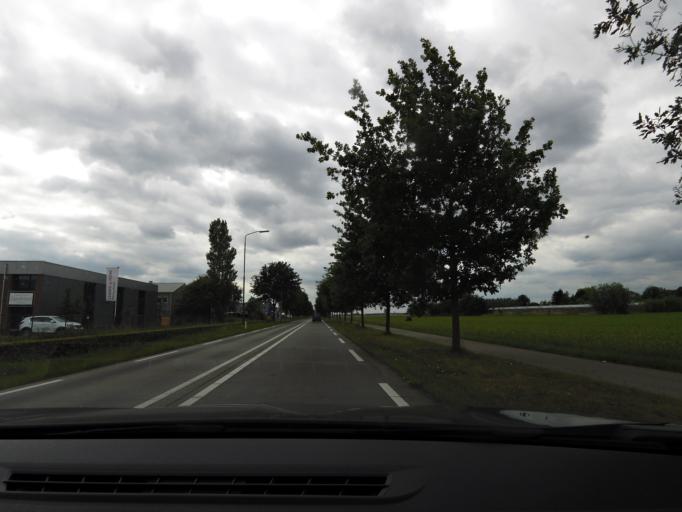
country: NL
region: North Brabant
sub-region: Gemeente Made en Drimmelen
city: Made
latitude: 51.6700
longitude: 4.7509
